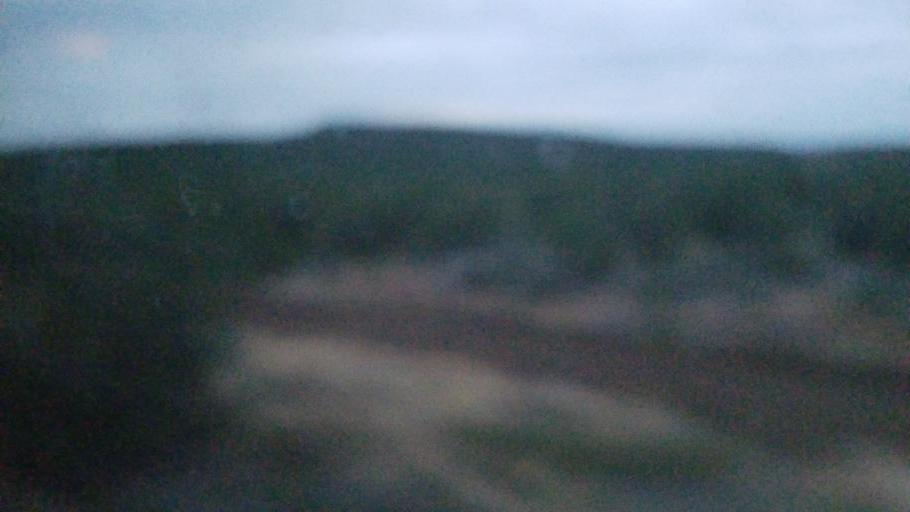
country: US
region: Arizona
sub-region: Yavapai County
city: Paulden
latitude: 35.2994
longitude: -112.6920
